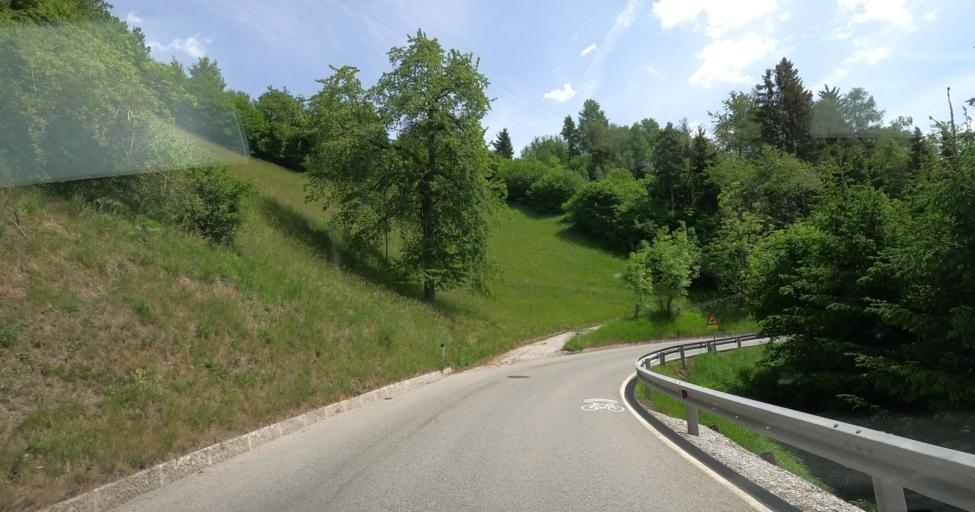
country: AT
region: Tyrol
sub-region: Politischer Bezirk Innsbruck Land
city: Patsch
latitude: 47.1948
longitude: 11.4248
